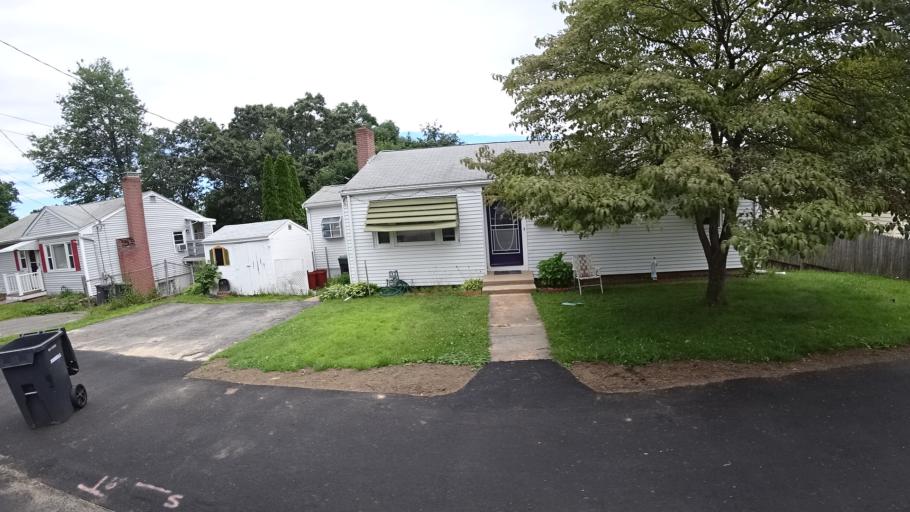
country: US
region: Massachusetts
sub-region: Norfolk County
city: Dedham
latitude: 42.2379
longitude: -71.1468
